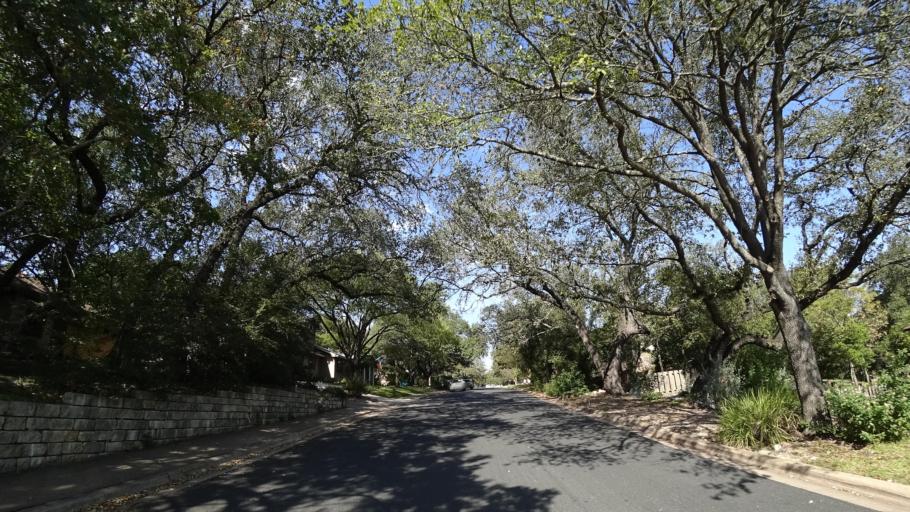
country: US
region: Texas
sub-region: Travis County
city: West Lake Hills
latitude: 30.3539
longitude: -97.7654
